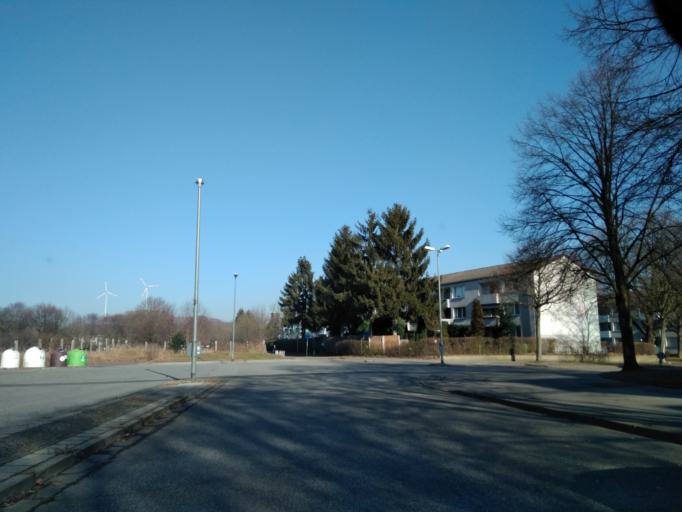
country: DE
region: North Rhine-Westphalia
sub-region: Regierungsbezirk Munster
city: Gladbeck
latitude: 51.5879
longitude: 7.0179
